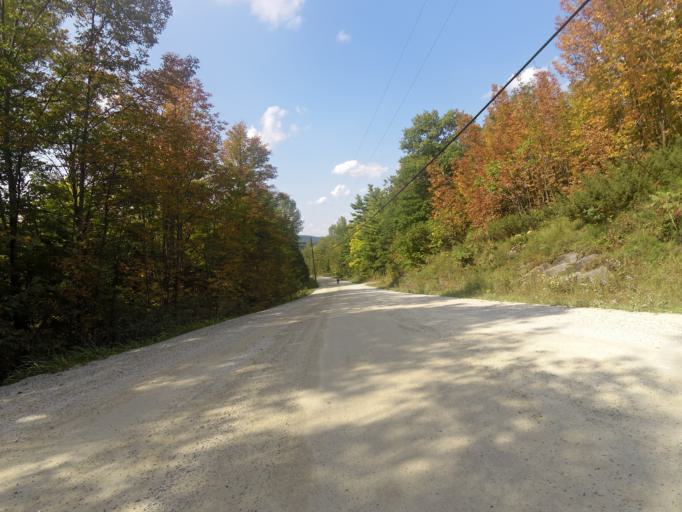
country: CA
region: Ontario
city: Renfrew
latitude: 45.1512
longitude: -76.6791
